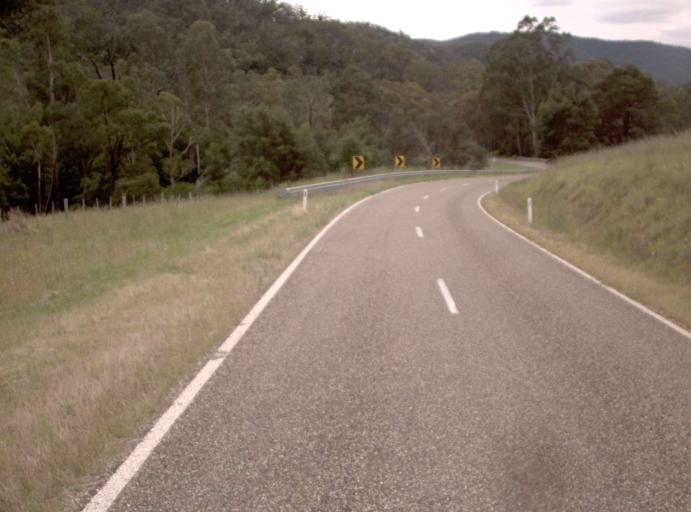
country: AU
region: Victoria
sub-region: East Gippsland
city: Bairnsdale
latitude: -37.5440
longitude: 147.2032
